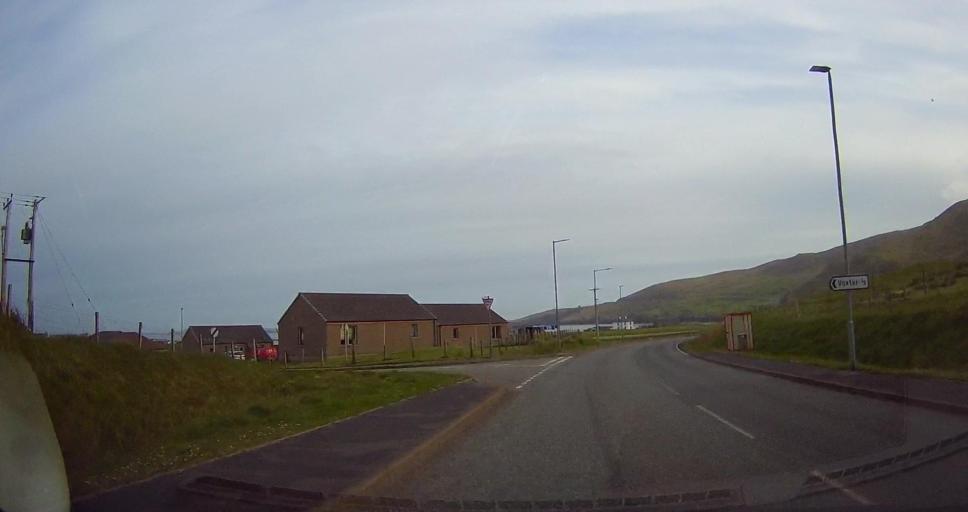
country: GB
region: Scotland
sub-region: Shetland Islands
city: Sandwick
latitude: 60.0391
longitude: -1.2297
